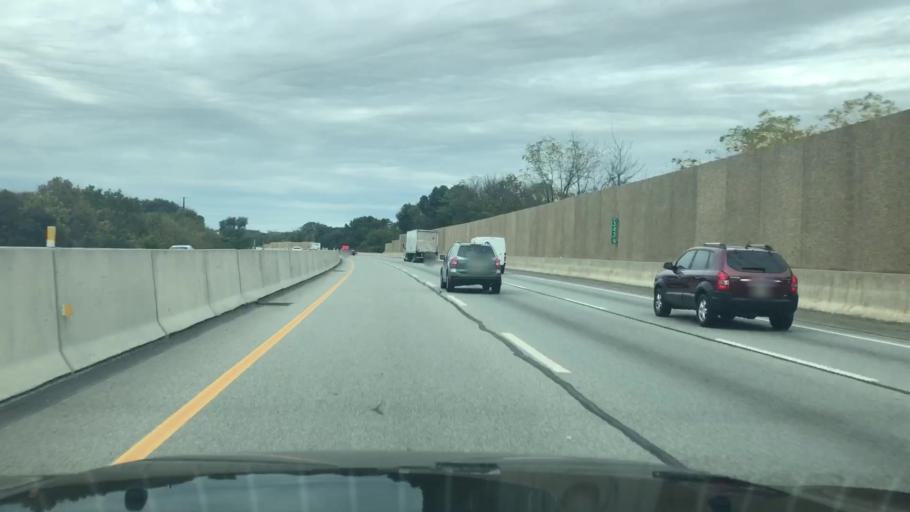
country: US
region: Pennsylvania
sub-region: Montgomery County
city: Hatboro
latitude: 40.1634
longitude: -75.1017
